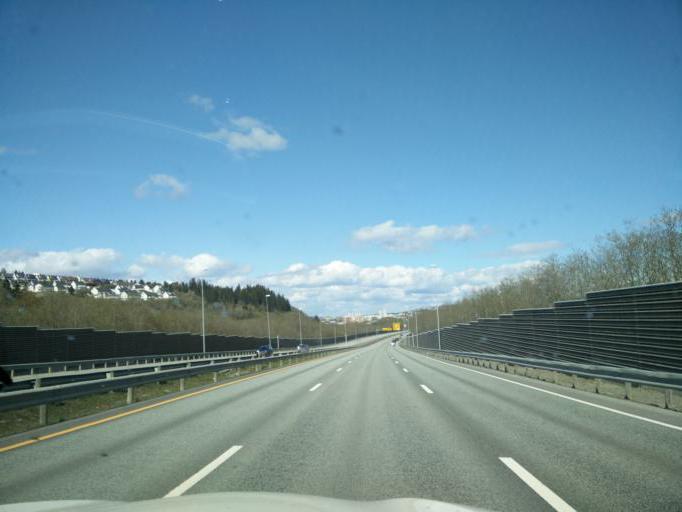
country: NO
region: Sor-Trondelag
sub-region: Trondheim
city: Trondheim
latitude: 63.3867
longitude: 10.3787
